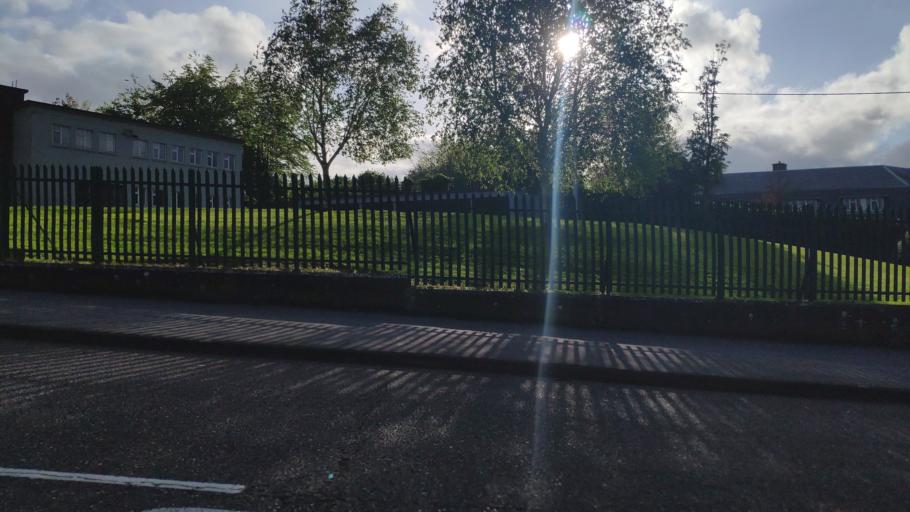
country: IE
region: Munster
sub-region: County Cork
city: Cork
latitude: 51.9127
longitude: -8.4833
